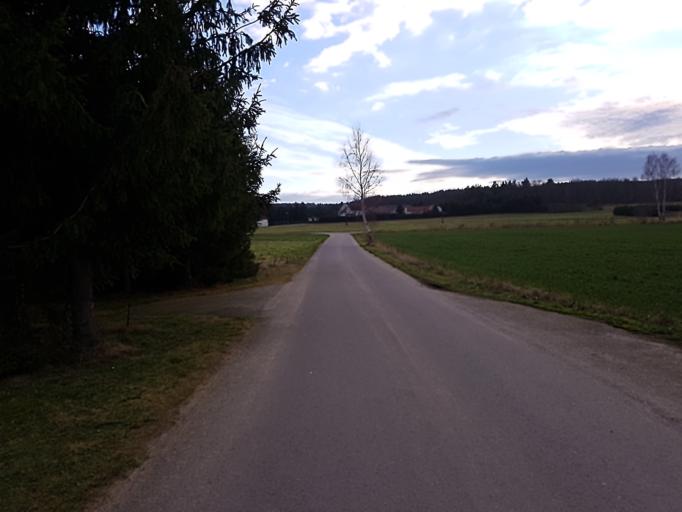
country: DE
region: Brandenburg
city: Groden
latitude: 51.4069
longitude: 13.5613
